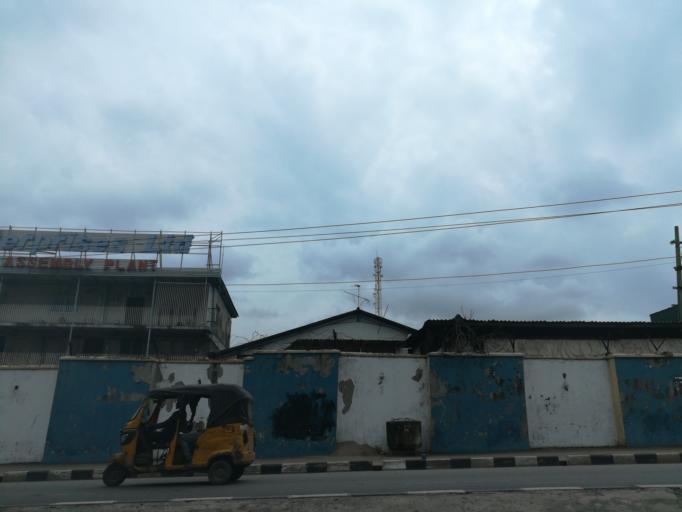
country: NG
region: Lagos
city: Ikeja
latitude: 6.6066
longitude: 3.3596
